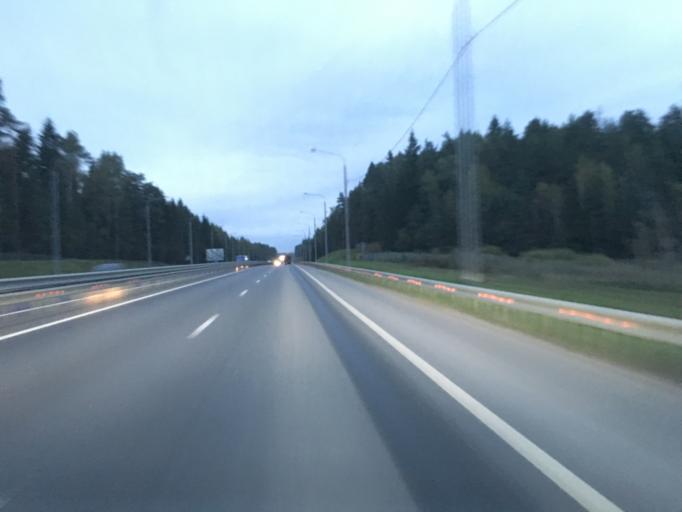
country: RU
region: Kaluga
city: Maloyaroslavets
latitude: 54.9298
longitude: 36.4131
